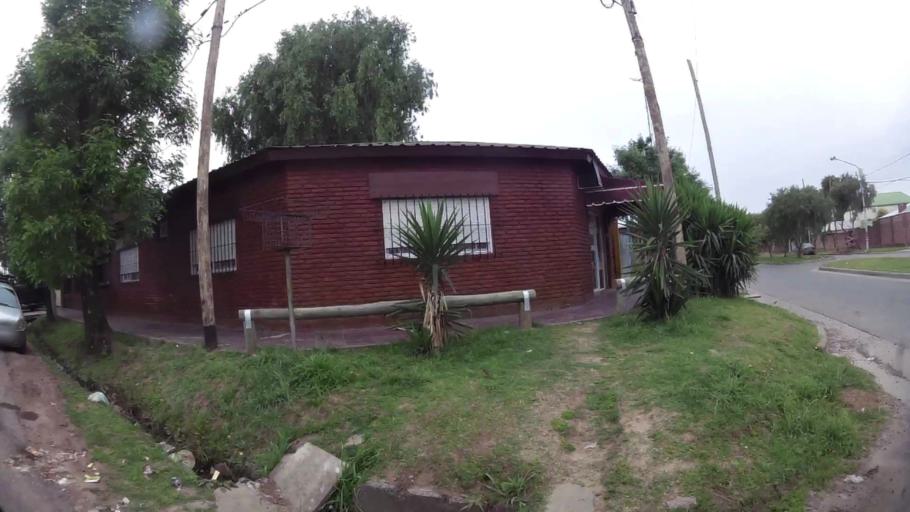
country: AR
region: Buenos Aires
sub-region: Partido de Campana
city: Campana
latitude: -34.1984
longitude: -58.9444
